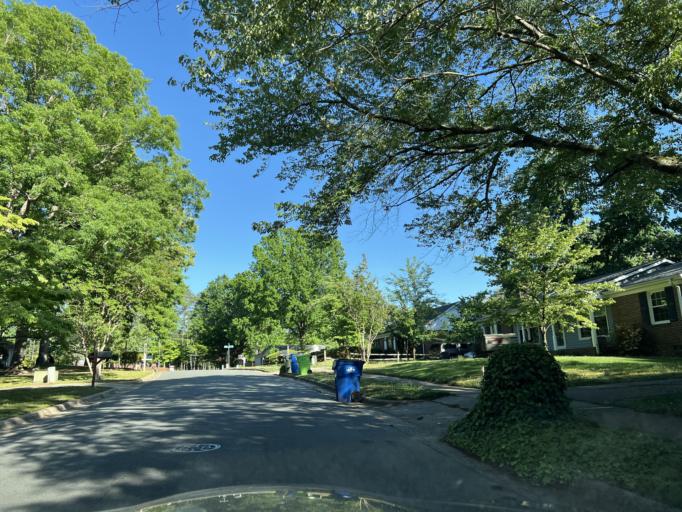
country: US
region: North Carolina
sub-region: Wake County
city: West Raleigh
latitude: 35.8638
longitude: -78.6389
